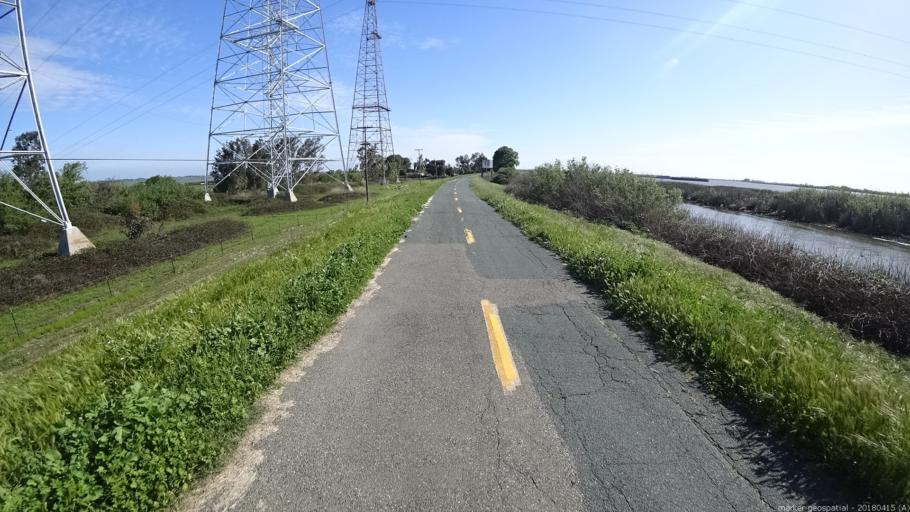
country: US
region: California
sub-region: Contra Costa County
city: Oakley
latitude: 38.0547
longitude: -121.6948
